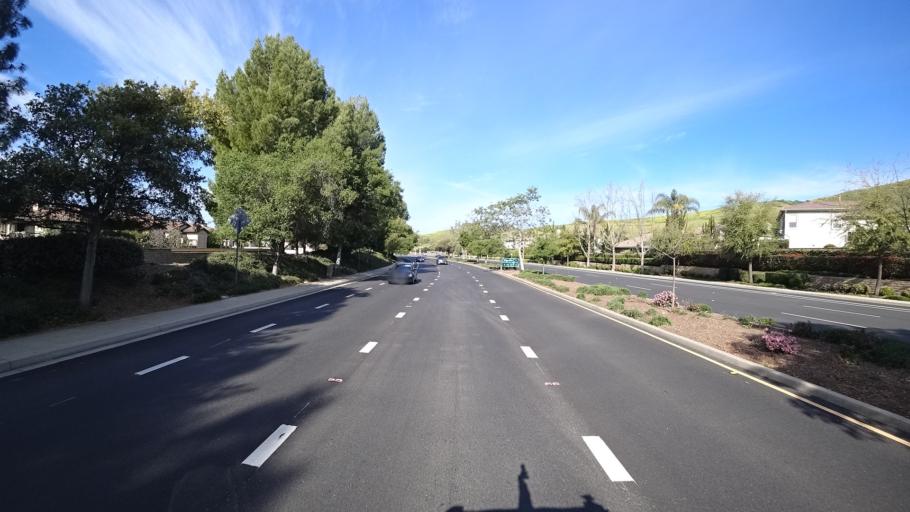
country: US
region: California
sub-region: Ventura County
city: Thousand Oaks
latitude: 34.2143
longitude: -118.8245
